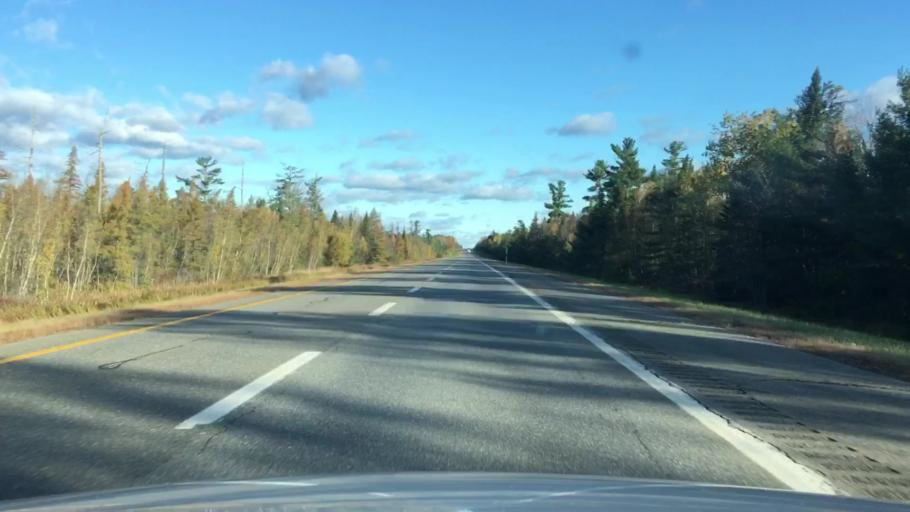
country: US
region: Maine
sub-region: Penobscot County
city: Greenbush
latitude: 45.0577
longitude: -68.6879
